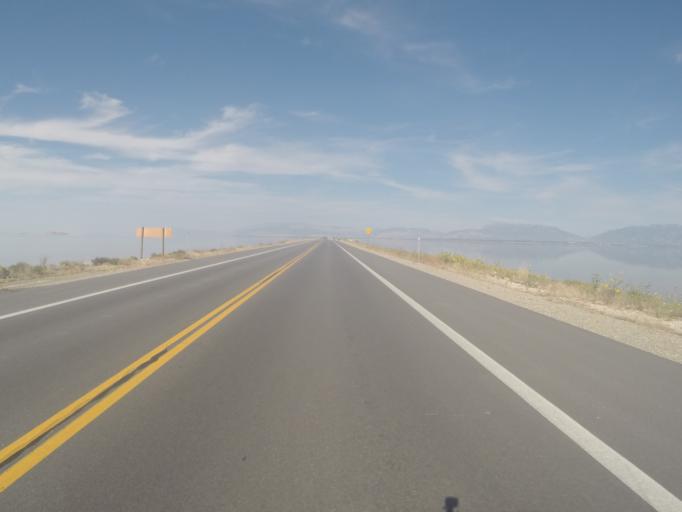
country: US
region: Utah
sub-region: Weber County
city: Hooper
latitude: 41.0619
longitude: -112.2350
